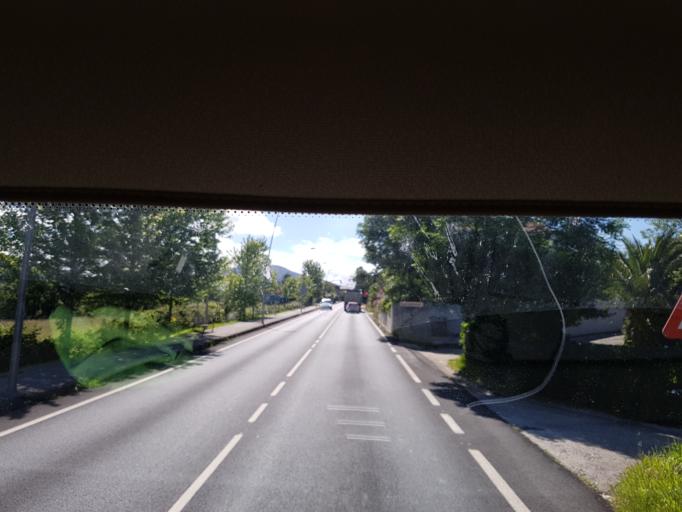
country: ES
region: Basque Country
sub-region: Bizkaia
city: San Julian de Muskiz
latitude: 43.3180
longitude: -3.0895
